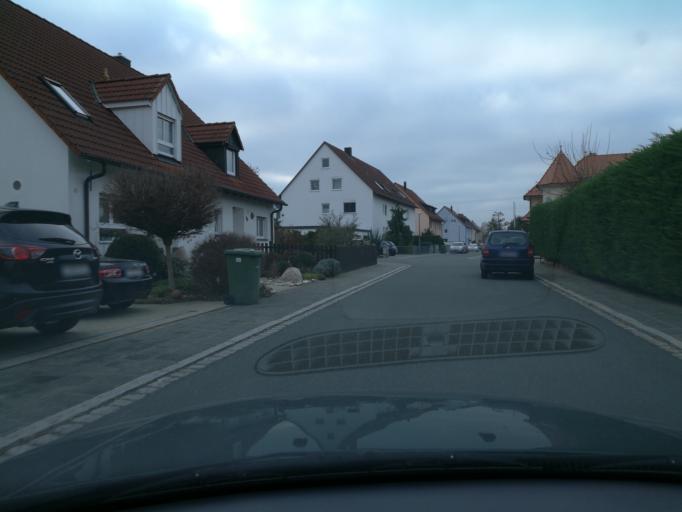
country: DE
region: Bavaria
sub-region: Regierungsbezirk Mittelfranken
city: Seukendorf
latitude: 49.4885
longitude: 10.8856
